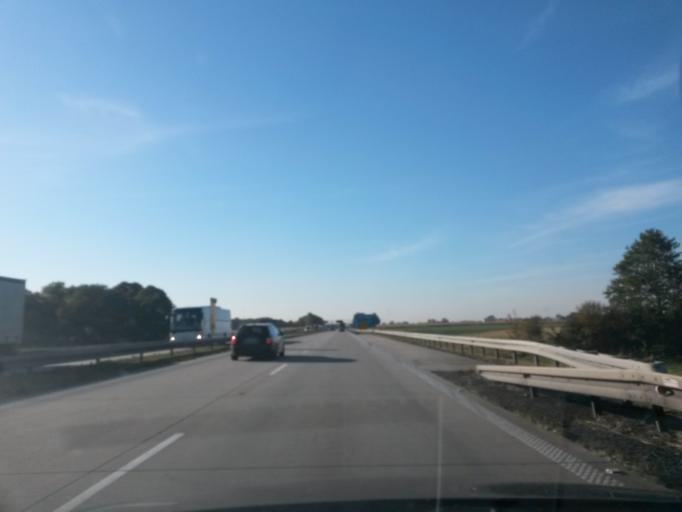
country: PL
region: Lower Silesian Voivodeship
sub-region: Powiat sredzki
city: Udanin
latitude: 51.0774
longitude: 16.4457
